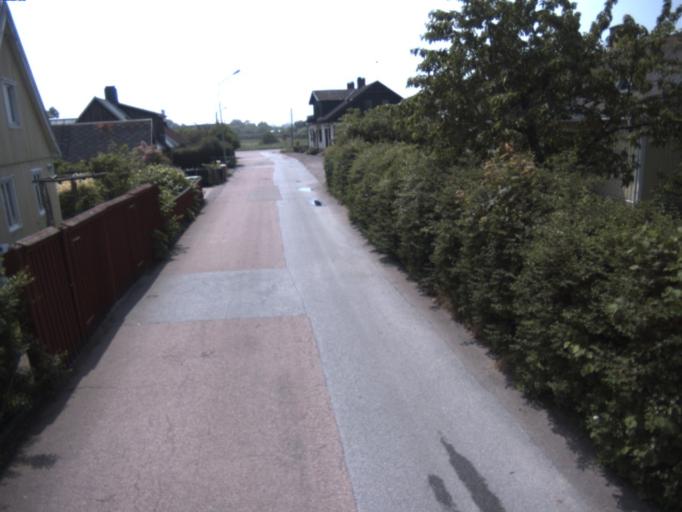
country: SE
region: Skane
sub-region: Angelholms Kommun
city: Strovelstorp
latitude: 56.2146
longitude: 12.7844
